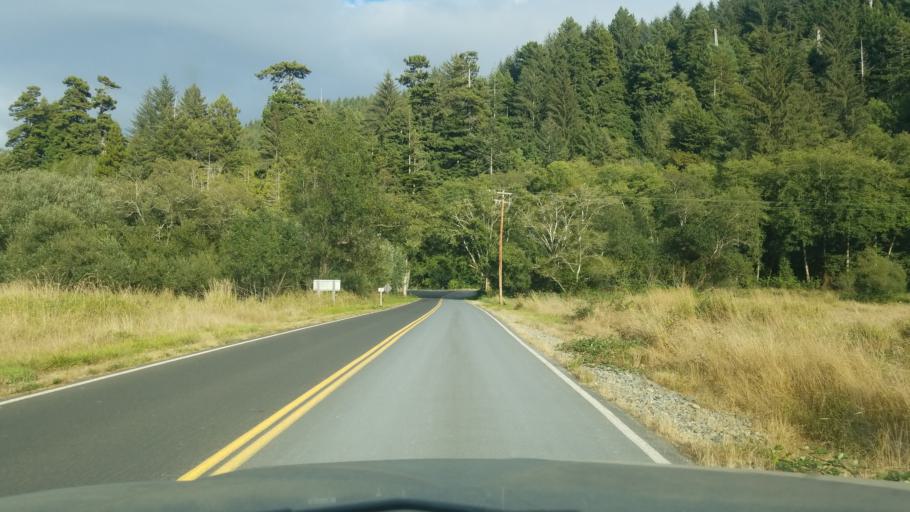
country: US
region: California
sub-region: Humboldt County
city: Westhaven-Moonstone
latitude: 41.3213
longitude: -124.0411
